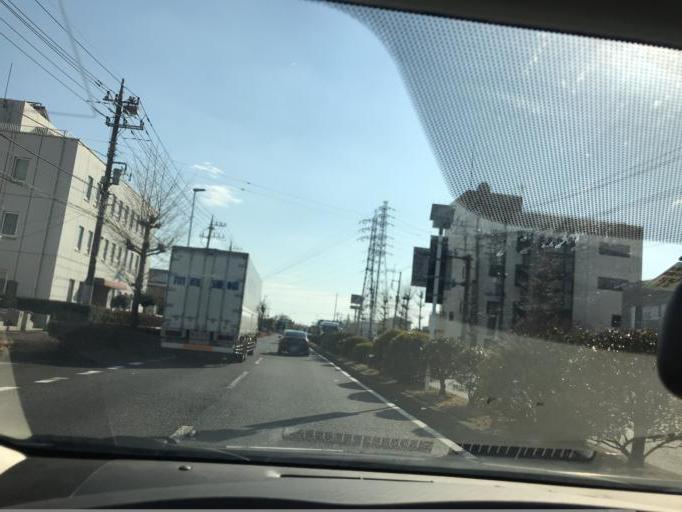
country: JP
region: Ibaraki
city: Mitsukaido
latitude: 36.0118
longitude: 139.9906
